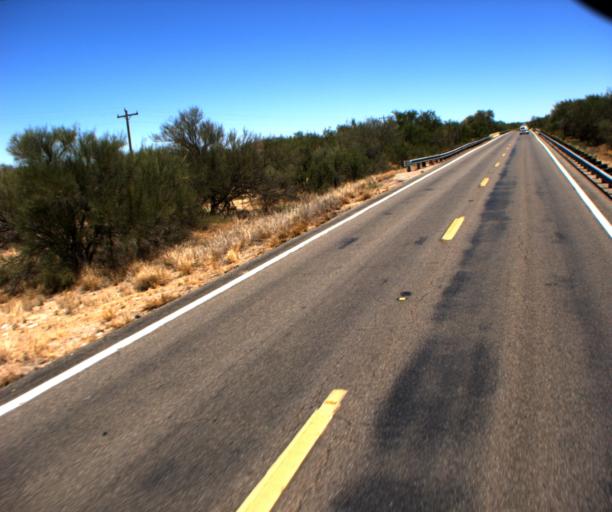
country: US
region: Arizona
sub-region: Pima County
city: Sells
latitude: 31.9527
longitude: -111.7595
